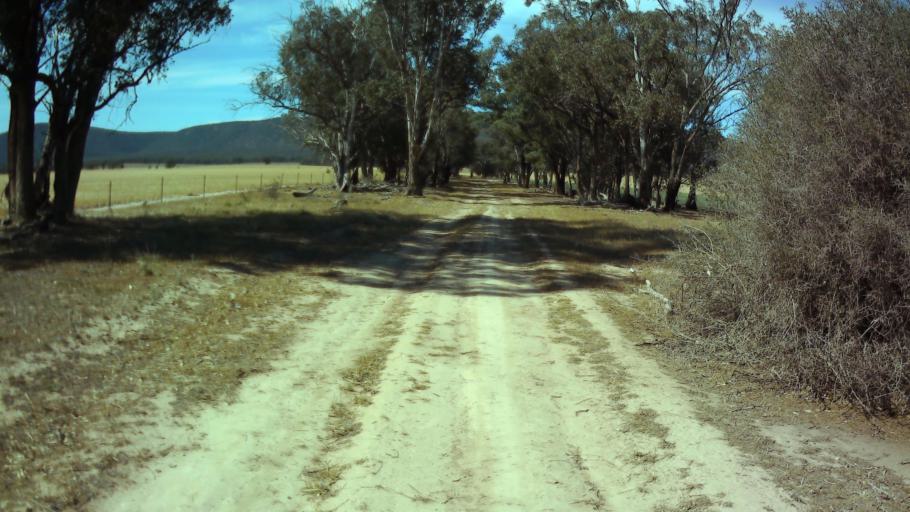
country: AU
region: New South Wales
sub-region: Weddin
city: Grenfell
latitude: -33.9426
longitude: 148.0473
